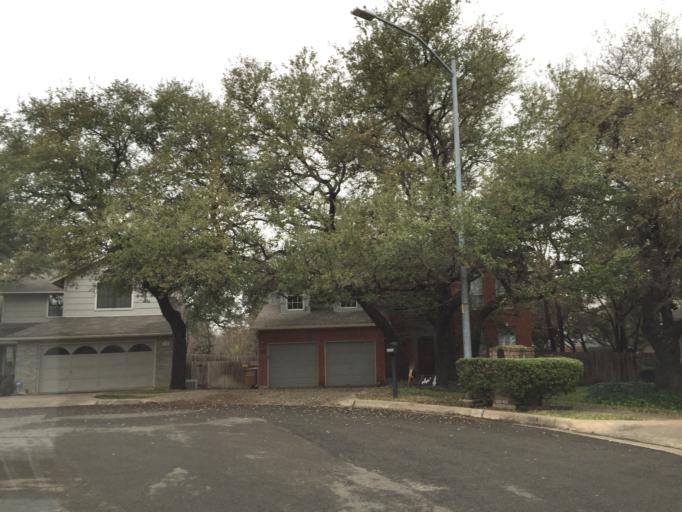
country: US
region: Texas
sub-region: Williamson County
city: Jollyville
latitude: 30.4167
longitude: -97.7341
